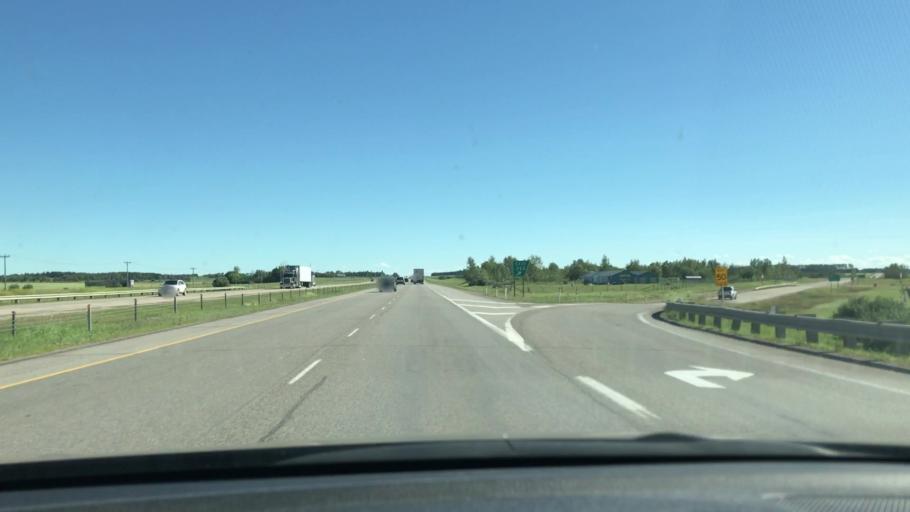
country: CA
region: Alberta
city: Olds
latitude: 51.9094
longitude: -114.0255
